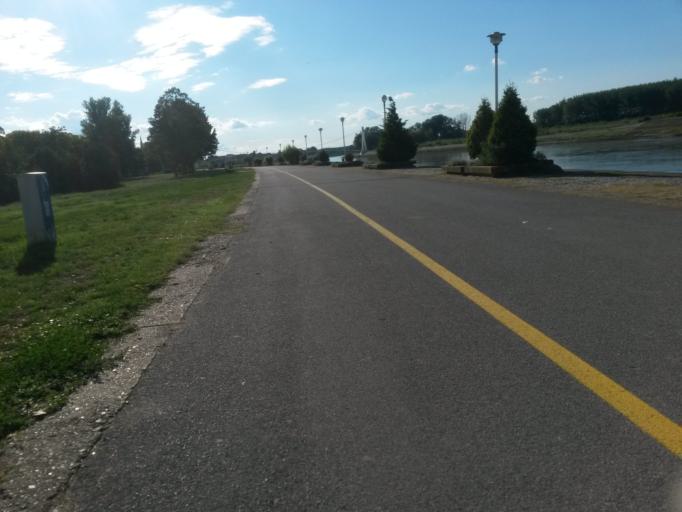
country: HR
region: Osjecko-Baranjska
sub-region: Grad Osijek
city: Osijek
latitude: 45.5633
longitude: 18.6942
